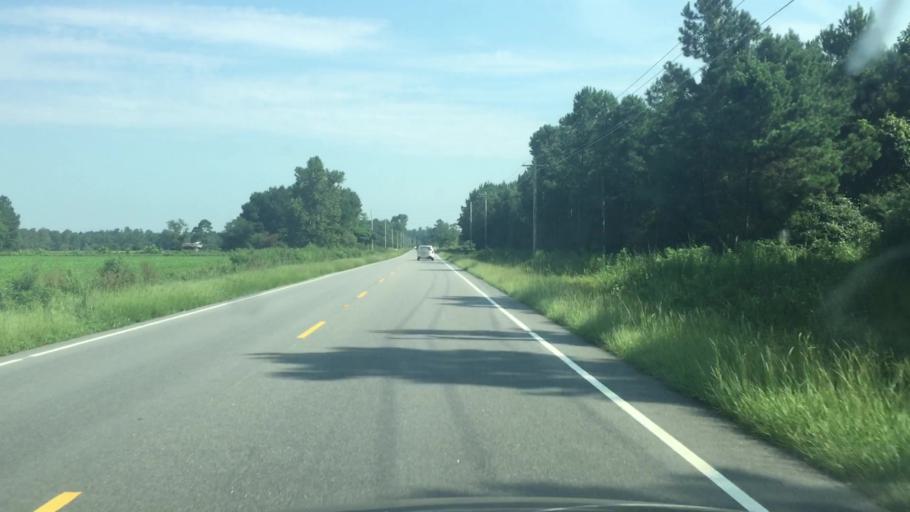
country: US
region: North Carolina
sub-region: Columbus County
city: Tabor City
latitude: 34.2229
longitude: -78.8241
